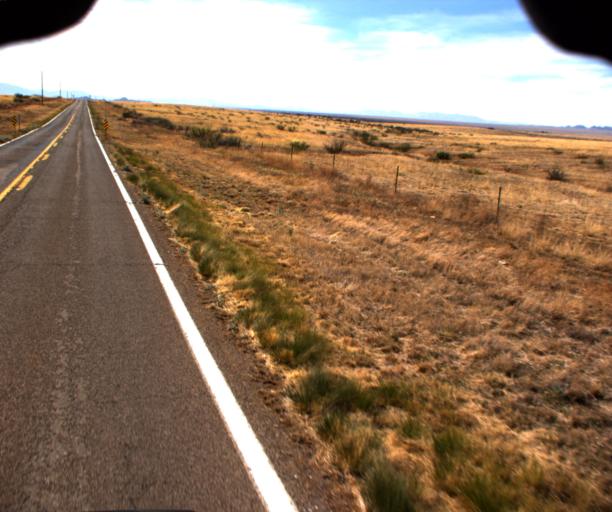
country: US
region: Arizona
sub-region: Cochise County
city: Willcox
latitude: 32.0068
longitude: -109.4291
